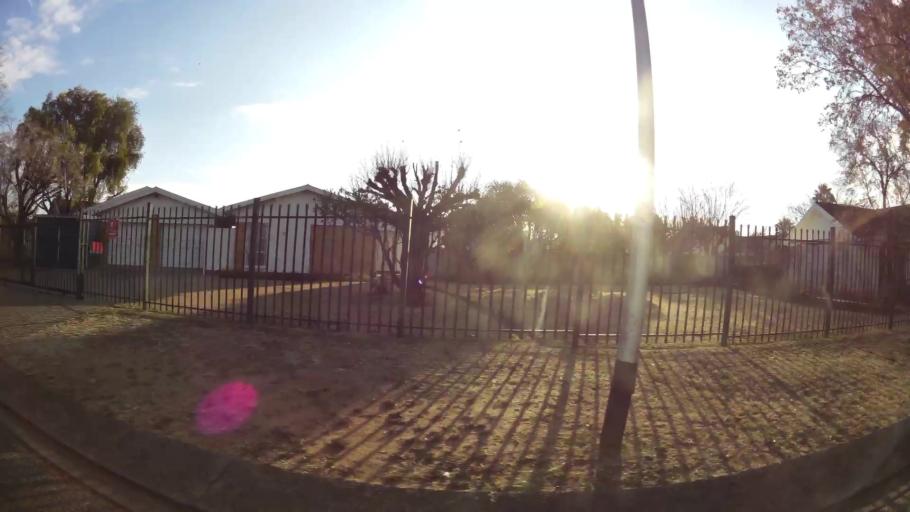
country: ZA
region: Orange Free State
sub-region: Mangaung Metropolitan Municipality
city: Bloemfontein
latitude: -29.1450
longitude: 26.1853
